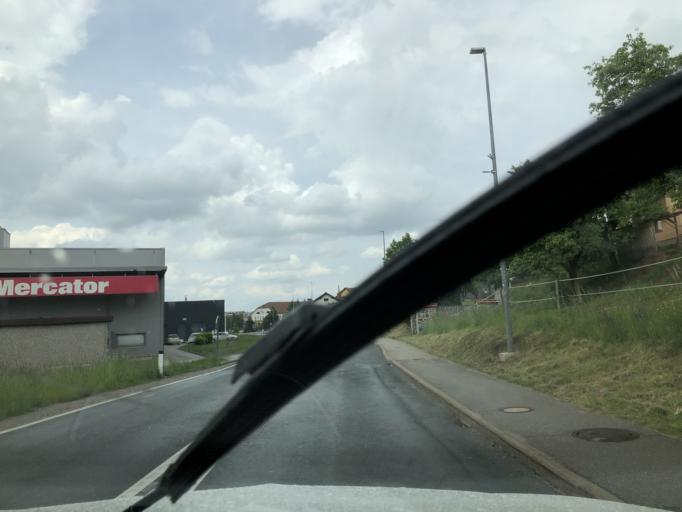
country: SI
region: Cerknica
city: Cerknica
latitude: 45.7894
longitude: 14.3691
